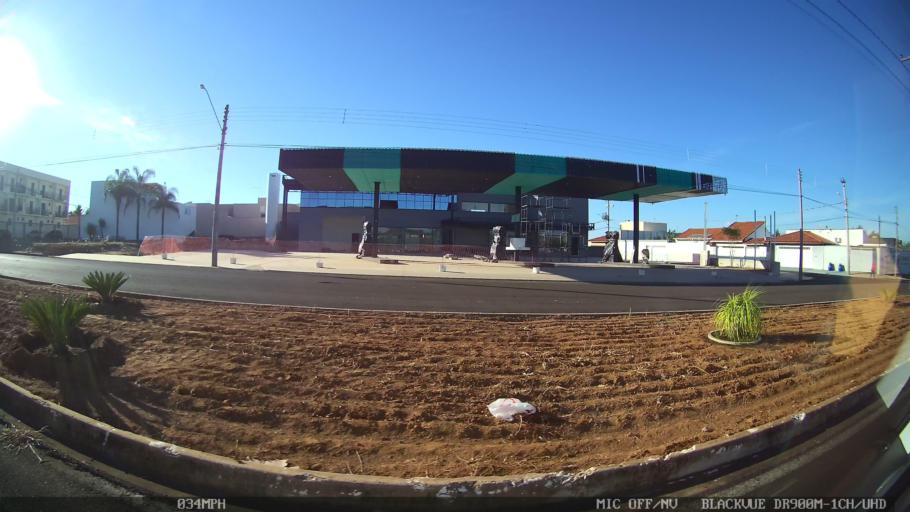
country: BR
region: Sao Paulo
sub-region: Franca
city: Franca
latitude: -20.5723
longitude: -47.4075
